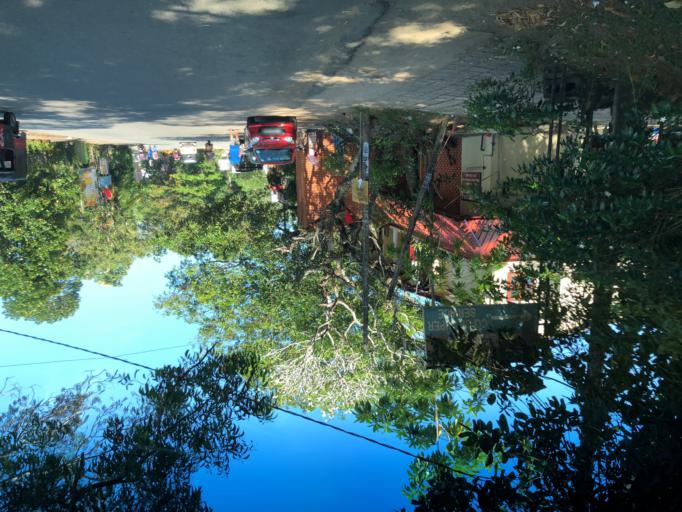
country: LK
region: Western
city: Homagama
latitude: 6.8151
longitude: 79.9720
